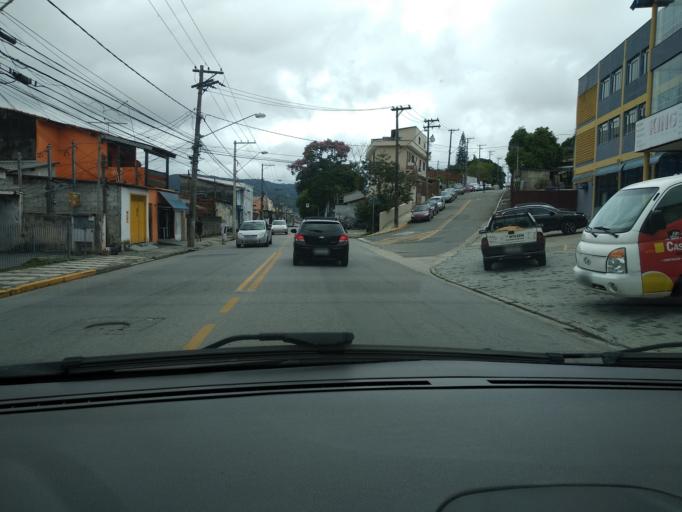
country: BR
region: Sao Paulo
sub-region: Mogi das Cruzes
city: Mogi das Cruzes
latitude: -23.5331
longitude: -46.1935
